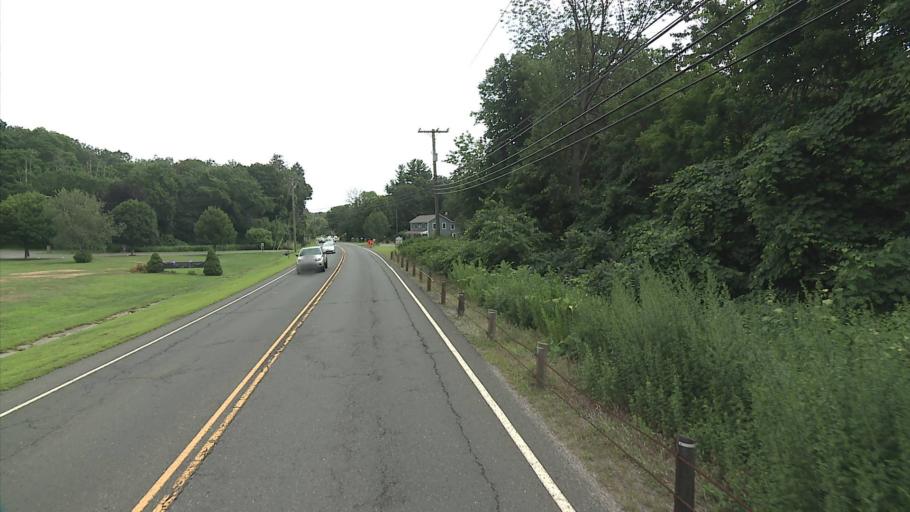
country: US
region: Connecticut
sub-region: New Haven County
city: Oxford
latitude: 41.4369
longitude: -73.1199
